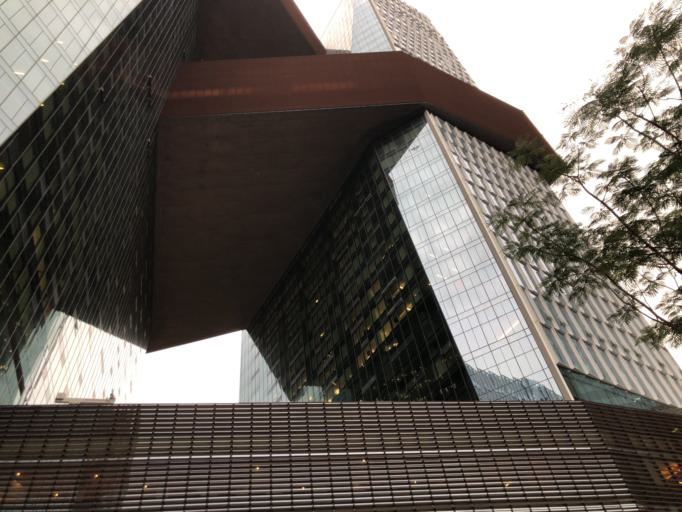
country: CN
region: Guangdong
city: Haikuotiankong
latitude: 22.5258
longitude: 113.9312
